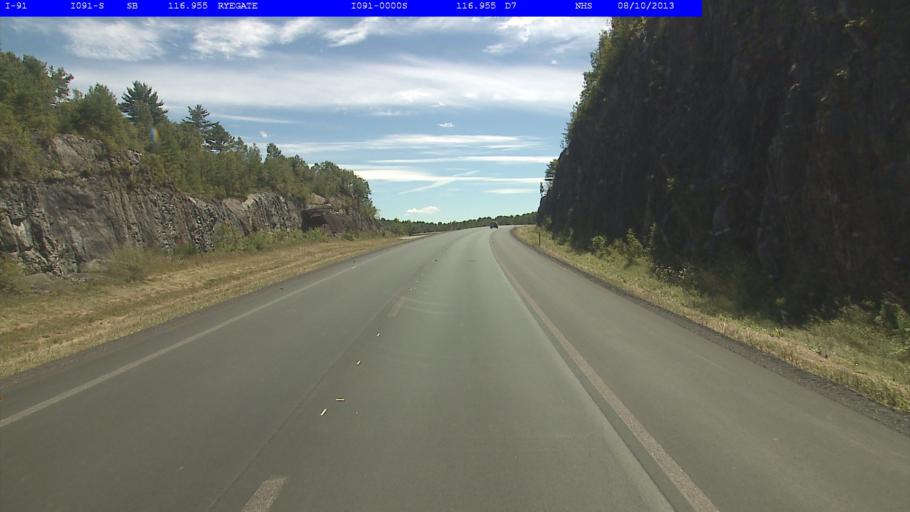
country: US
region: New Hampshire
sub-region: Grafton County
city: Woodsville
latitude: 44.2521
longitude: -72.0617
